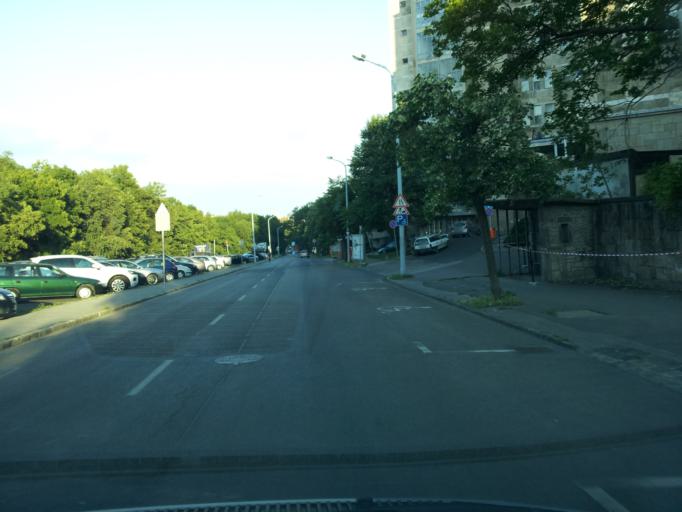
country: HU
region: Budapest
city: Budapest XII. keruelet
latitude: 47.5120
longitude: 19.0042
